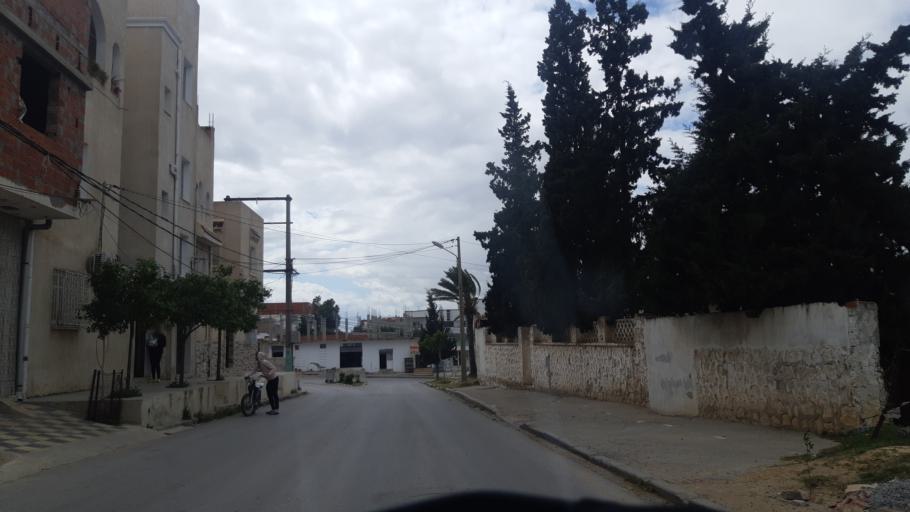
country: TN
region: Susah
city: Akouda
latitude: 35.8632
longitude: 10.5404
